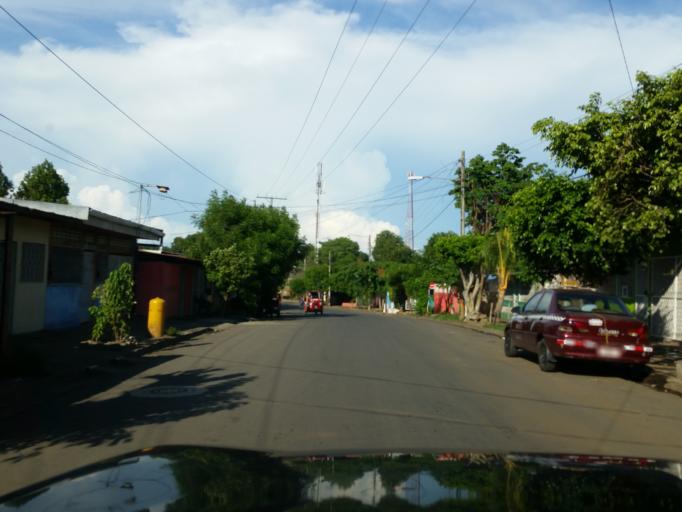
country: NI
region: Managua
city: Managua
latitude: 12.1038
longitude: -86.2227
